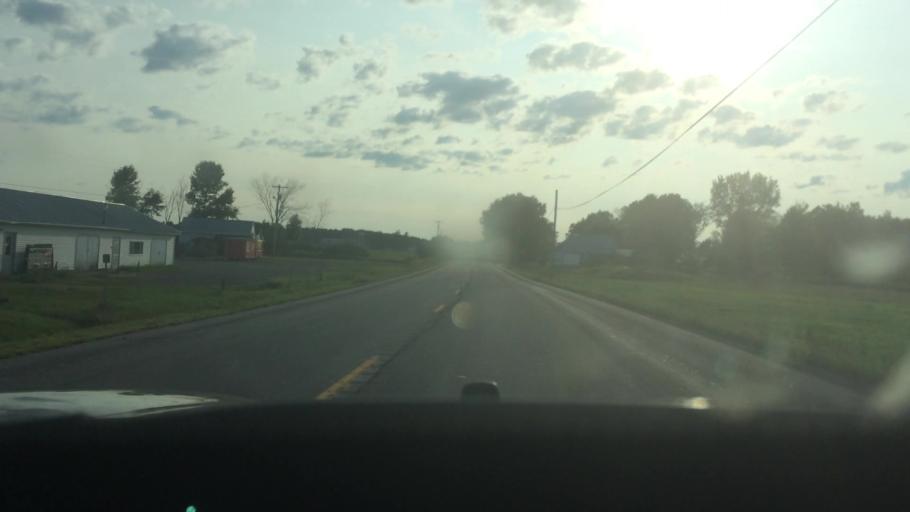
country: US
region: New York
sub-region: St. Lawrence County
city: Ogdensburg
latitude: 44.6741
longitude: -75.4130
